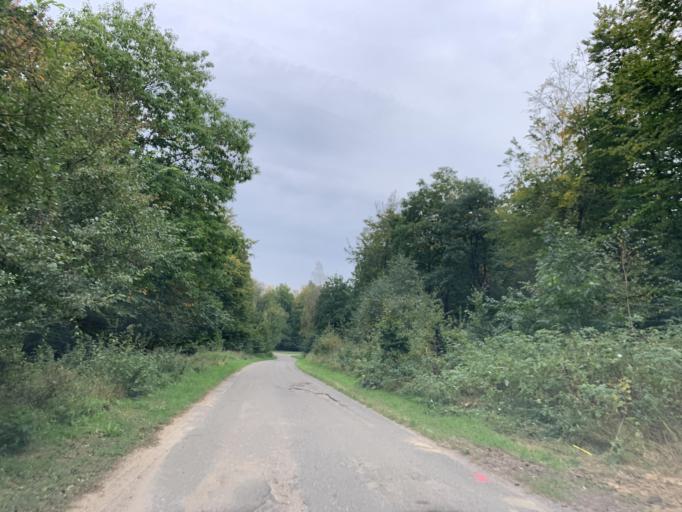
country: DE
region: Mecklenburg-Vorpommern
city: Woldegk
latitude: 53.3274
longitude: 13.5973
